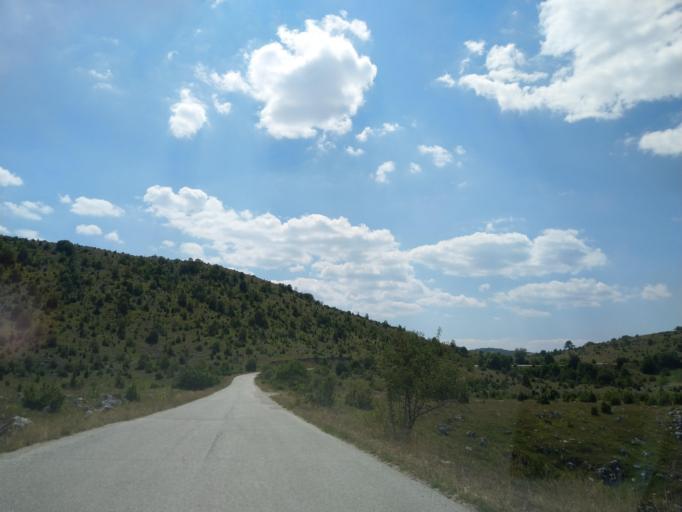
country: RS
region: Central Serbia
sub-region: Zlatiborski Okrug
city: Nova Varos
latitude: 43.4281
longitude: 19.9469
